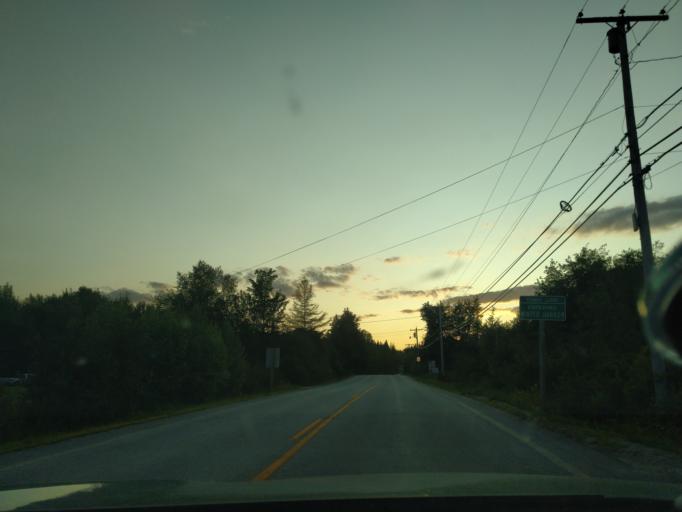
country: US
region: Maine
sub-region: Hancock County
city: Gouldsboro
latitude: 44.3907
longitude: -68.0452
